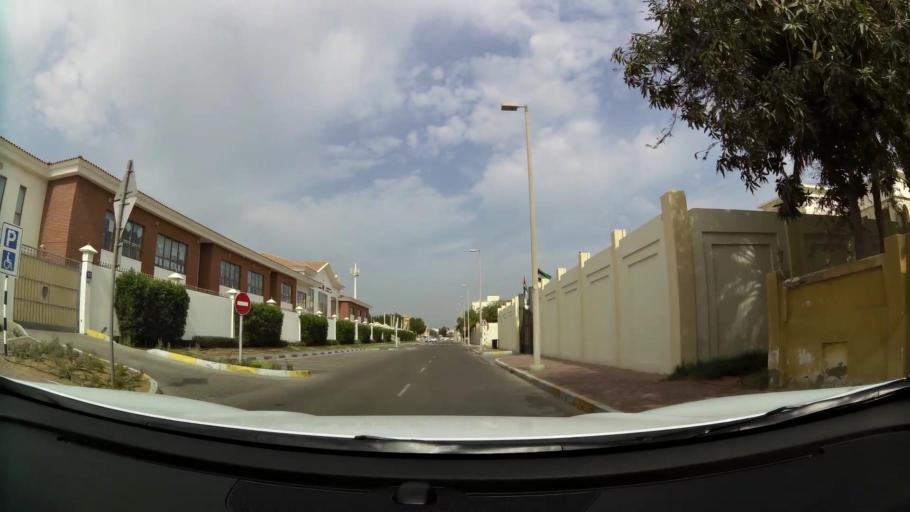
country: AE
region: Abu Dhabi
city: Abu Dhabi
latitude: 24.4535
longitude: 54.3727
